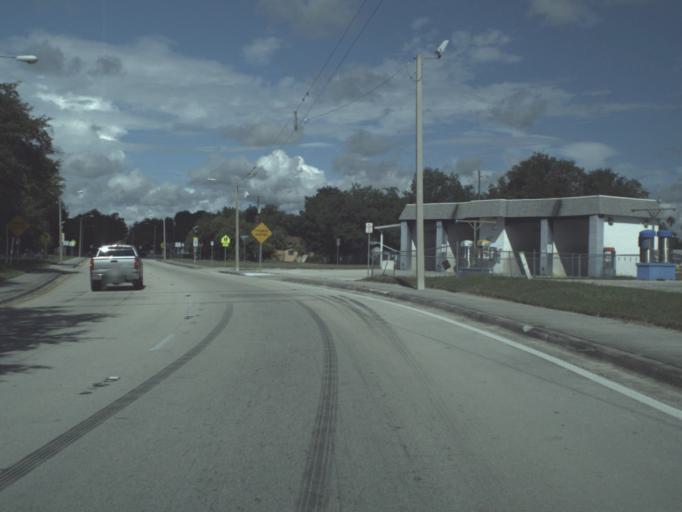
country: US
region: Florida
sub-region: DeSoto County
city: Arcadia
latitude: 27.2134
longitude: -81.8510
